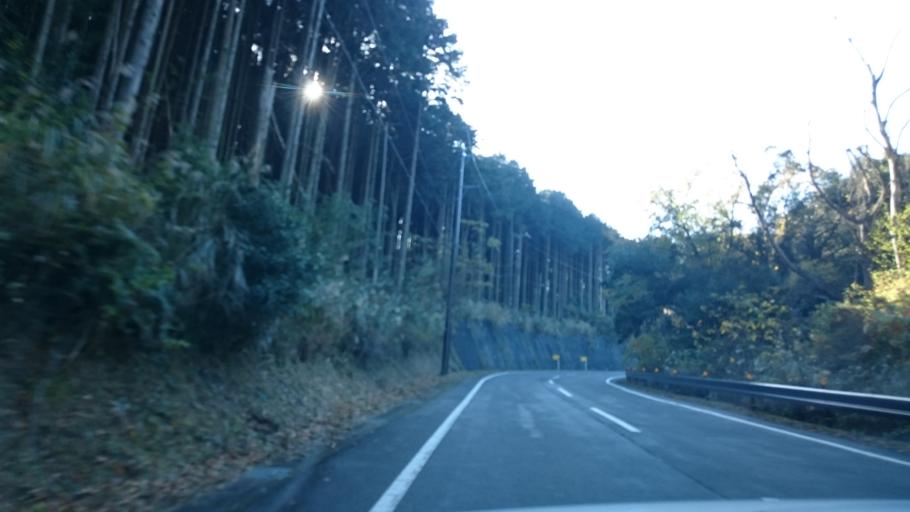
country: JP
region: Shizuoka
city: Heda
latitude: 35.0001
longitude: 138.8196
